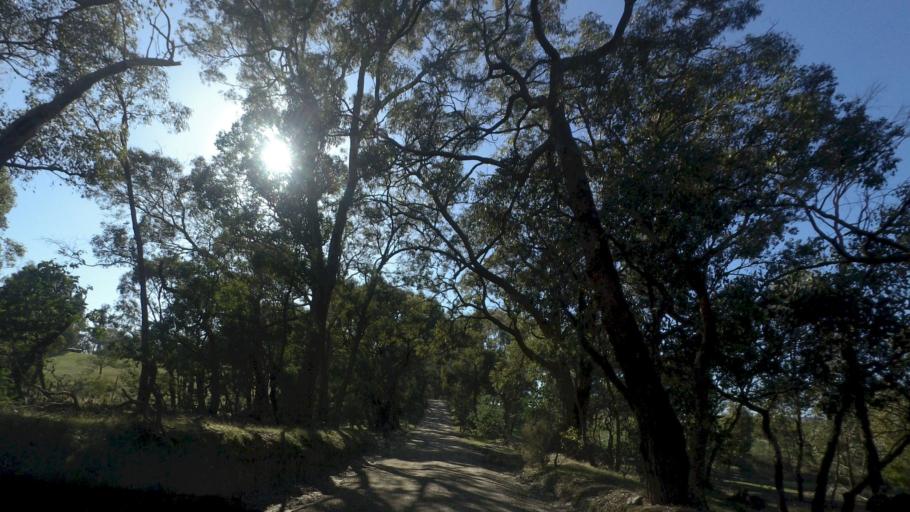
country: AU
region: Victoria
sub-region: Mount Alexander
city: Castlemaine
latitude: -37.1289
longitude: 144.4073
